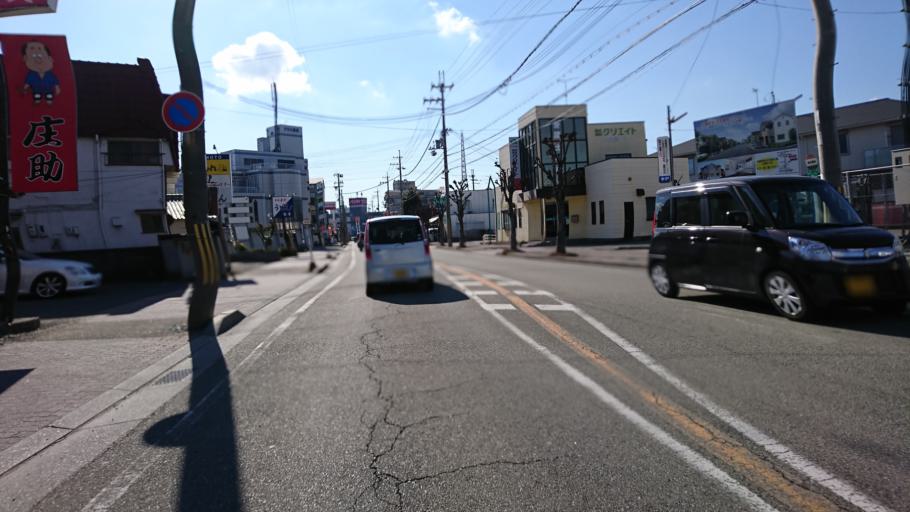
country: JP
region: Hyogo
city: Kakogawacho-honmachi
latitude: 34.7737
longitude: 134.8034
